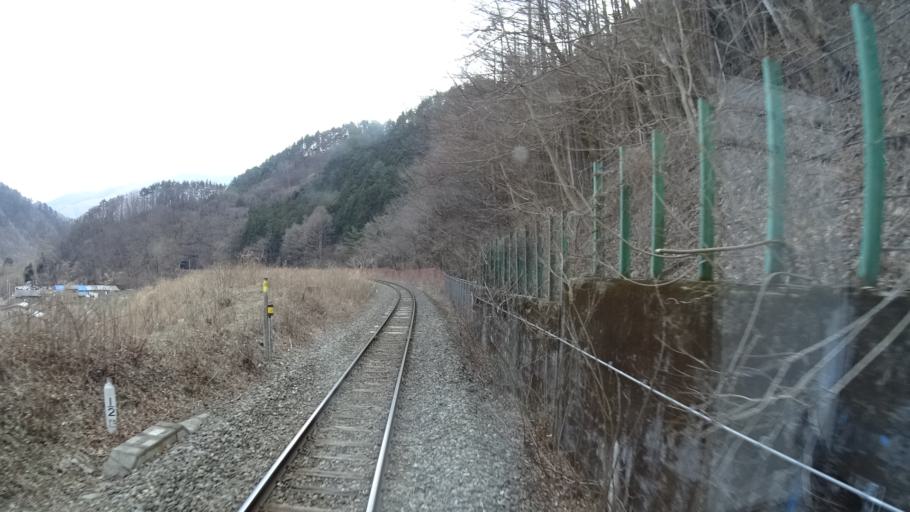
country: JP
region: Iwate
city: Kamaishi
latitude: 39.2655
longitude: 141.7254
